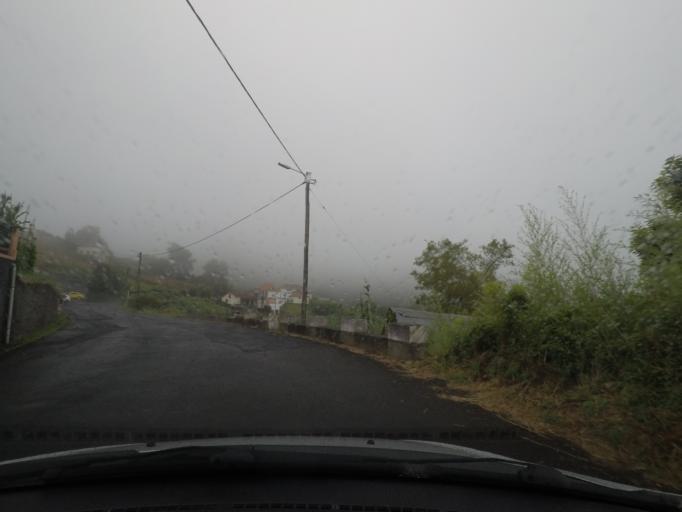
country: PT
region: Madeira
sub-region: Santana
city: Santana
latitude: 32.7952
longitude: -16.8754
